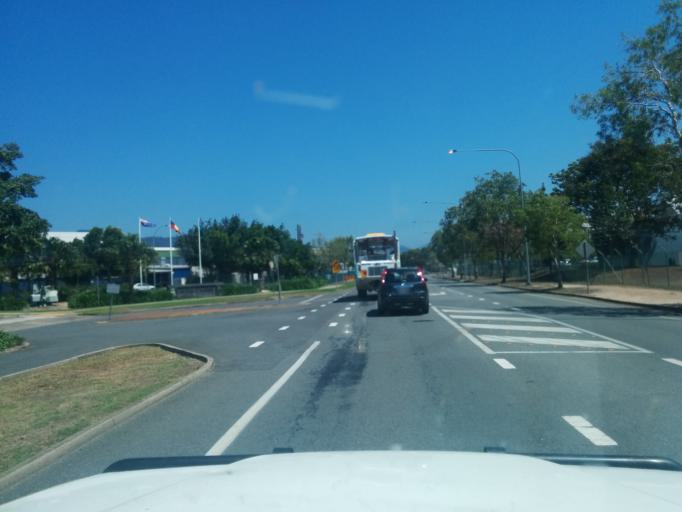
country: AU
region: Queensland
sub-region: Cairns
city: Cairns
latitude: -16.9362
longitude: 145.7767
